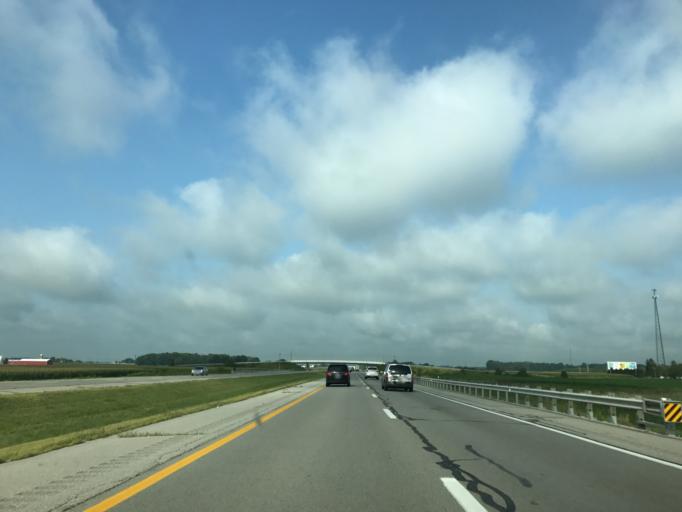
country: US
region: Ohio
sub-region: Williams County
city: West Unity
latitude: 41.6062
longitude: -84.4539
